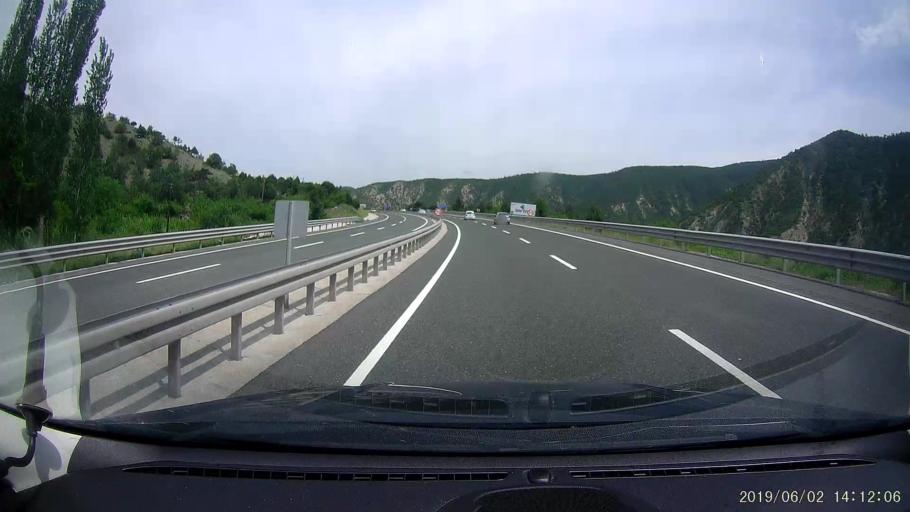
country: TR
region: Cankiri
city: Yaprakli
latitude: 40.9113
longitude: 33.8020
